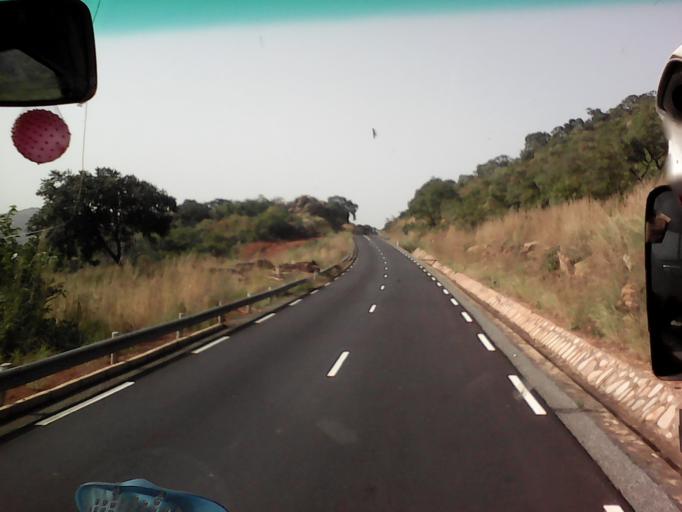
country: TG
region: Kara
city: Bafilo
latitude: 9.2460
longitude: 1.2147
